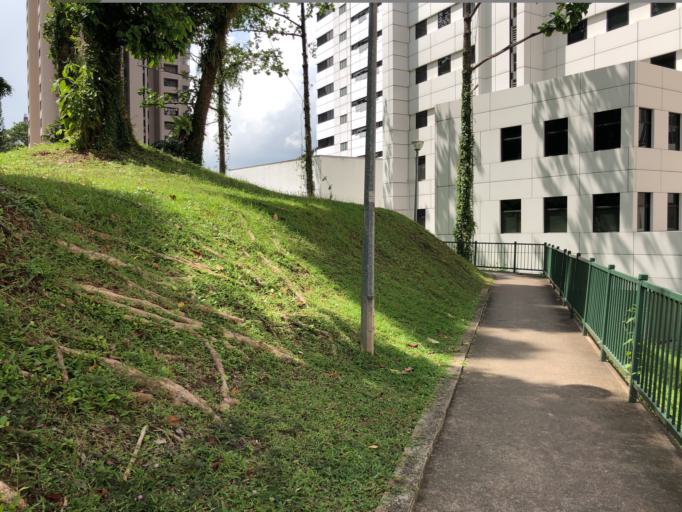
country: SG
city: Singapore
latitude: 1.2868
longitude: 103.8407
